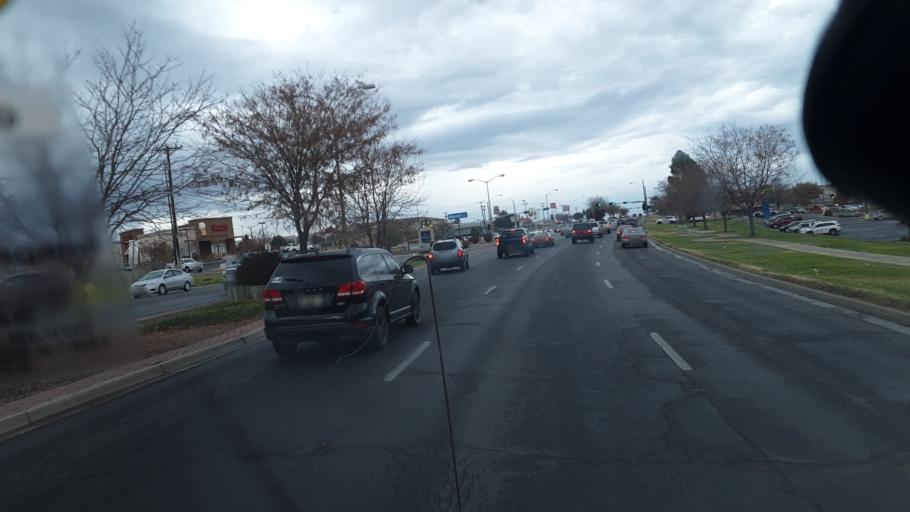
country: US
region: New Mexico
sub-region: San Juan County
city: Farmington
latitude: 36.7643
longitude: -108.1532
